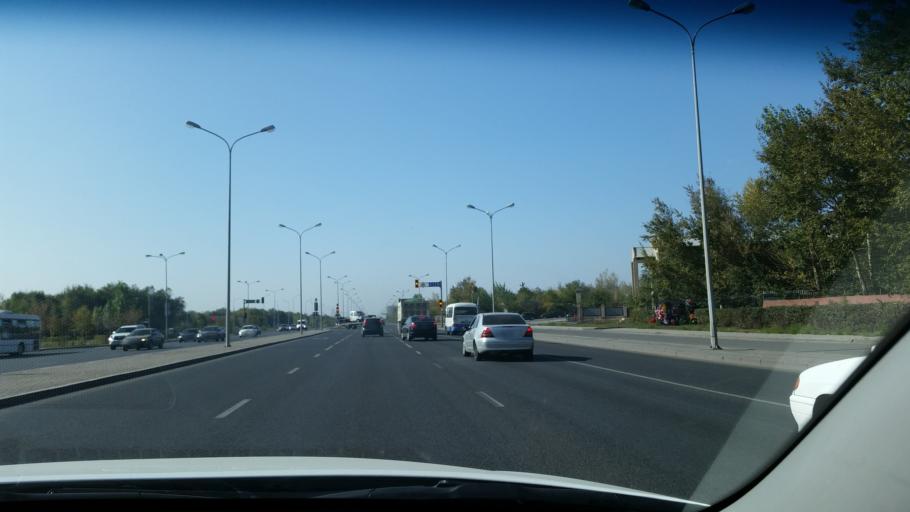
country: KZ
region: Astana Qalasy
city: Astana
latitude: 51.1836
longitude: 71.3657
